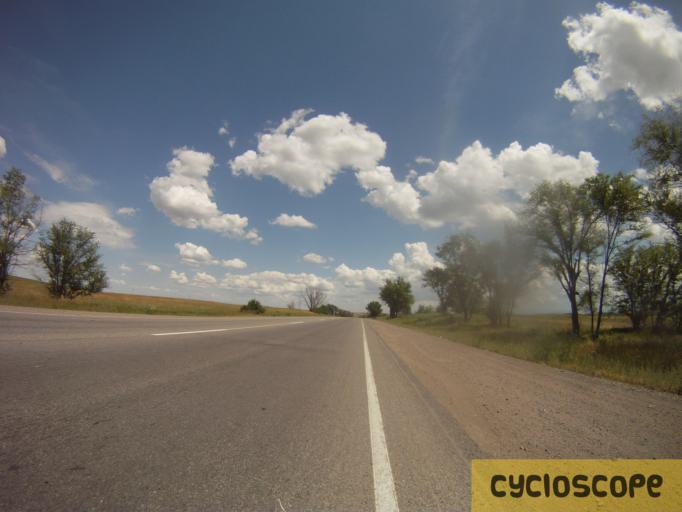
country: KG
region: Chuy
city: Bystrovka
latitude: 43.3148
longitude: 76.1503
